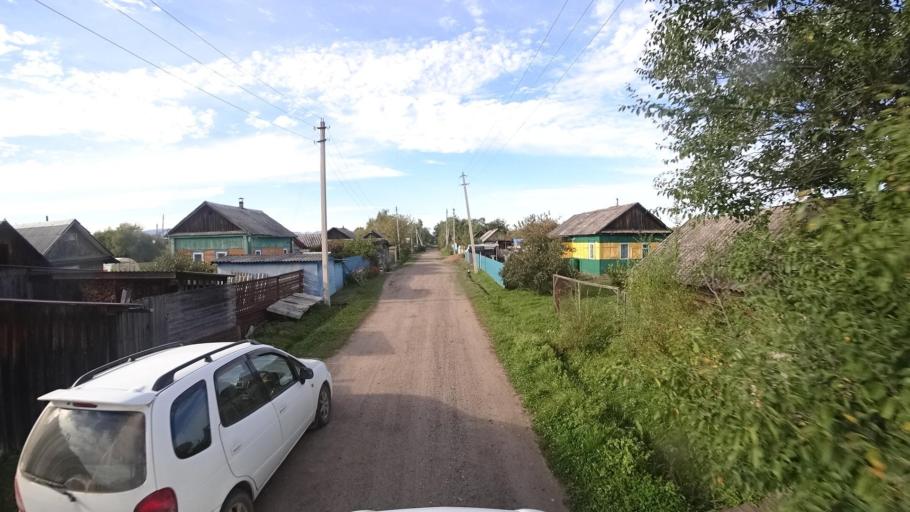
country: RU
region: Primorskiy
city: Dostoyevka
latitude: 44.2909
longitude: 133.4303
